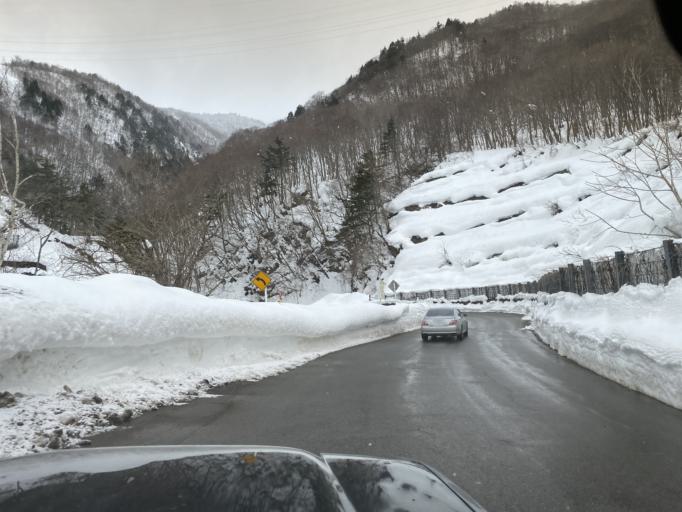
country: JP
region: Gifu
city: Takayama
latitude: 36.1136
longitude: 136.9209
